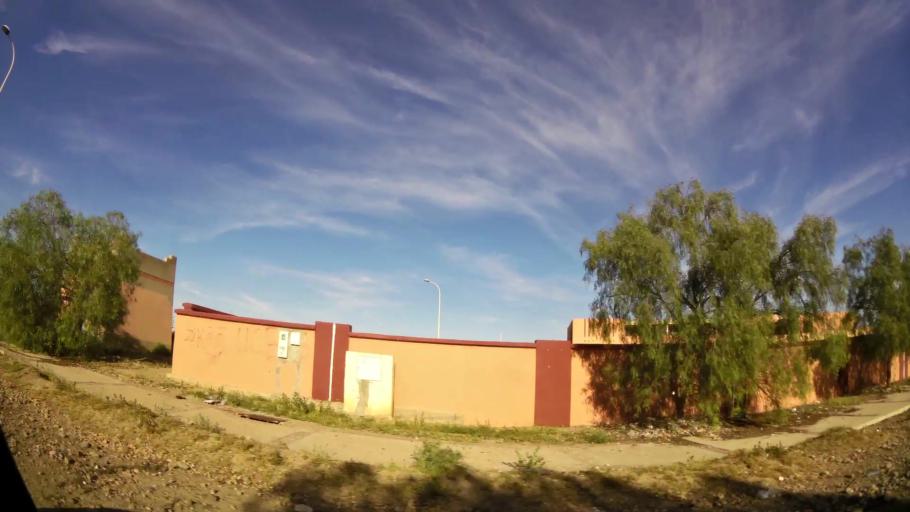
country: MA
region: Marrakech-Tensift-Al Haouz
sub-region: Marrakech
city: Marrakesh
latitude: 31.7552
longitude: -8.0952
